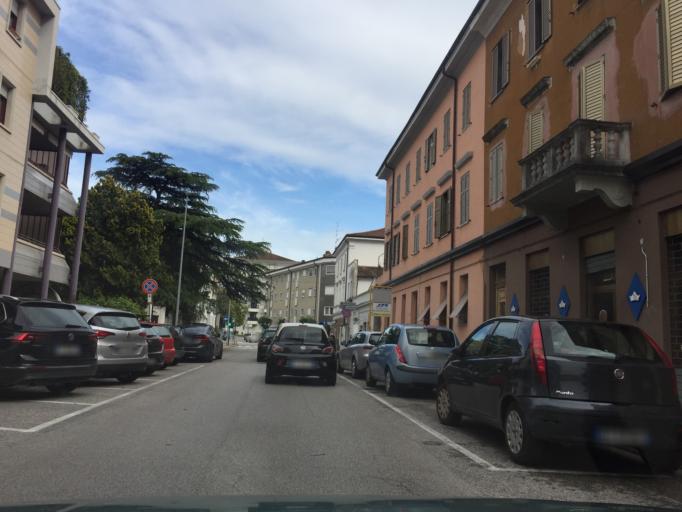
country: IT
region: Friuli Venezia Giulia
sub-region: Provincia di Gorizia
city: Monfalcone
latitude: 45.8076
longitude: 13.5295
